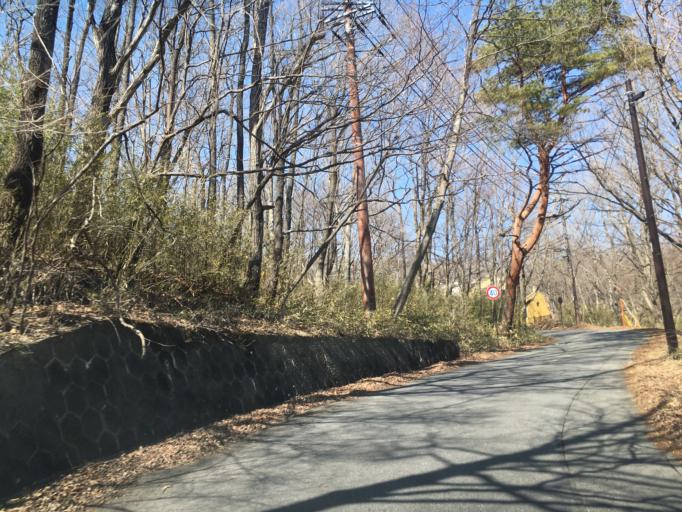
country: JP
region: Tochigi
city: Kuroiso
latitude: 37.0751
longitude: 140.0038
